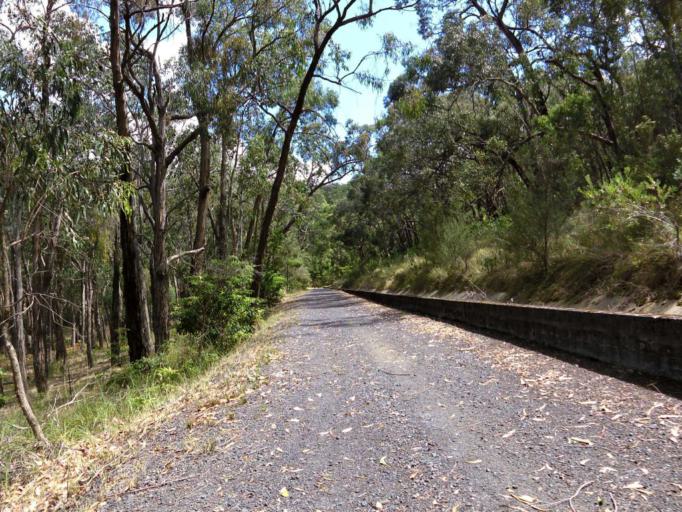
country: AU
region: Victoria
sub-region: Cardinia
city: Officer
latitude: -38.0358
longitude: 145.4425
